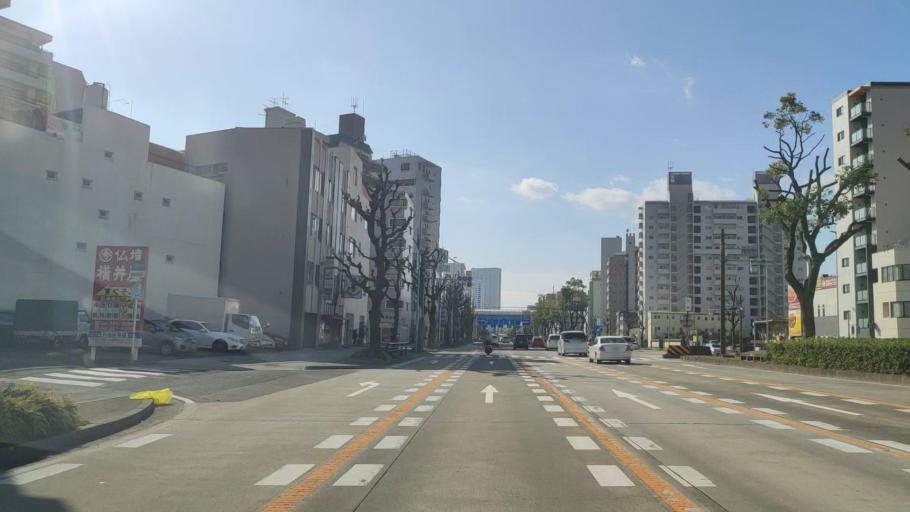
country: JP
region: Aichi
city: Nagoya-shi
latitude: 35.1544
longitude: 136.8988
